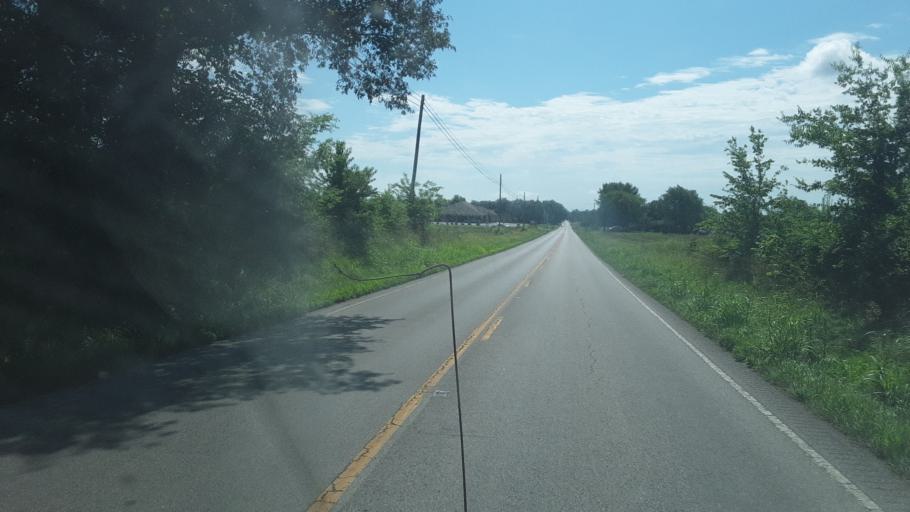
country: US
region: Kentucky
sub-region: Todd County
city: Elkton
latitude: 36.8155
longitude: -87.1799
